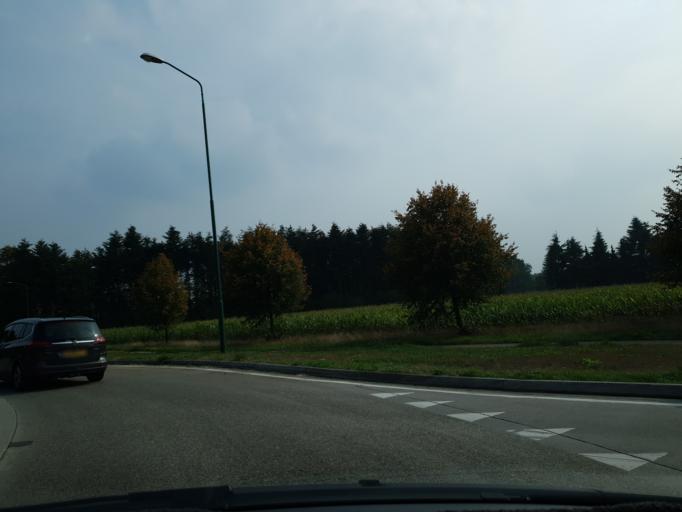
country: NL
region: North Brabant
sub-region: Bergeijk
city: Bergeyk
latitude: 51.3385
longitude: 5.3951
